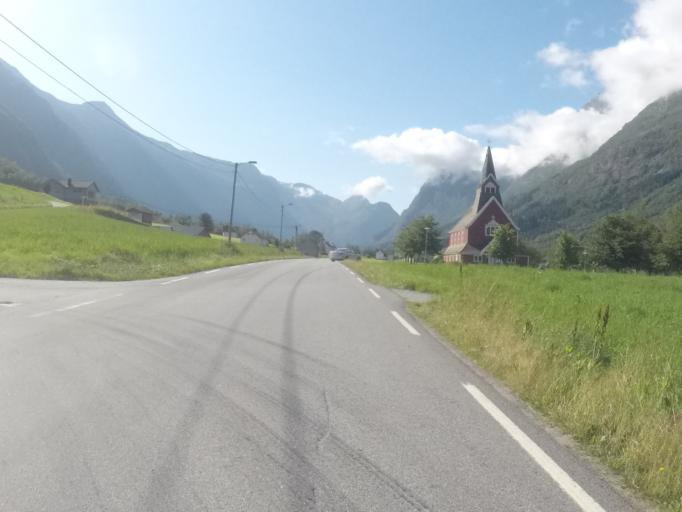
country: NO
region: Sogn og Fjordane
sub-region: Stryn
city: Stryn
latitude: 61.8286
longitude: 6.8084
